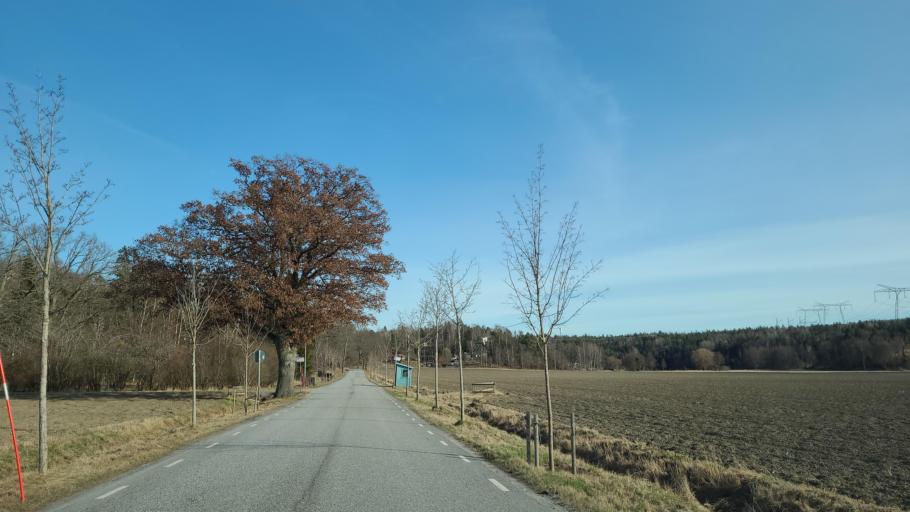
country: SE
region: Stockholm
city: Stenhamra
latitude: 59.2805
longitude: 17.6703
